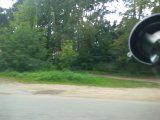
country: RU
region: Moskovskaya
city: Zhukovskiy
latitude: 55.5870
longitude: 38.1490
